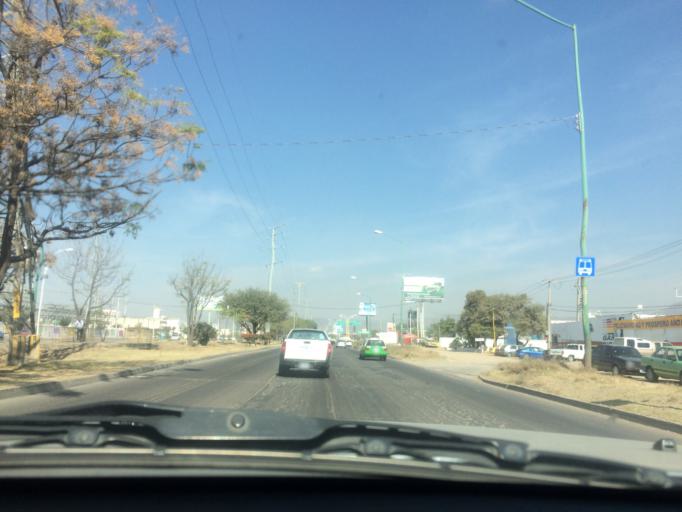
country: MX
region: Guanajuato
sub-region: Leon
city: Medina
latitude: 21.1346
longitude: -101.6308
